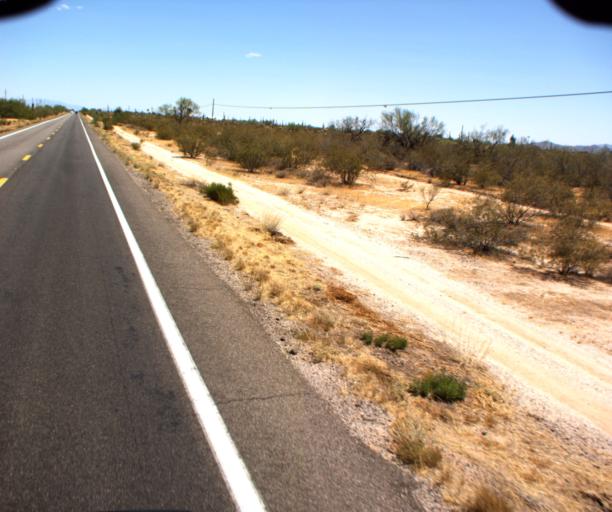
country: US
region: Arizona
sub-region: Pinal County
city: Florence
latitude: 32.9707
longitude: -111.3452
